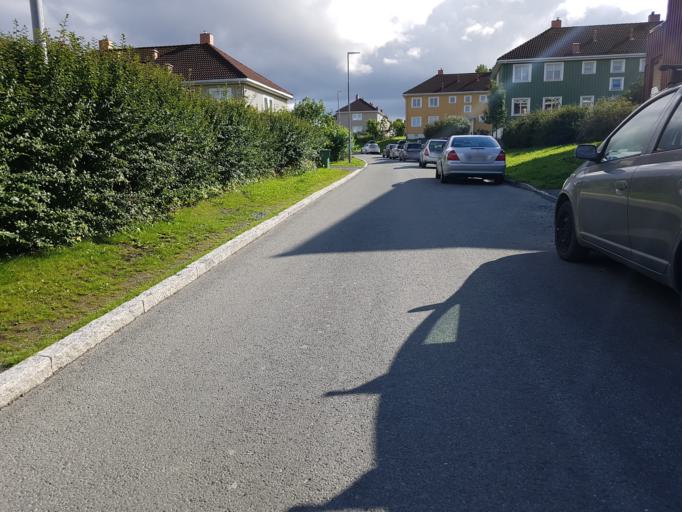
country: NO
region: Sor-Trondelag
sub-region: Trondheim
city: Trondheim
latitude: 63.4265
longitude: 10.4374
